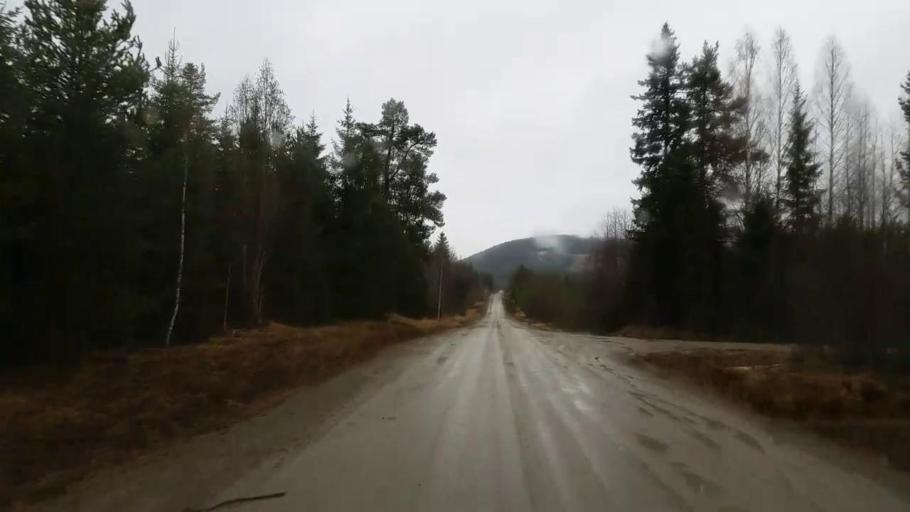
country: SE
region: Gaevleborg
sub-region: Ljusdals Kommun
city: Farila
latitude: 62.0792
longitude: 15.7739
